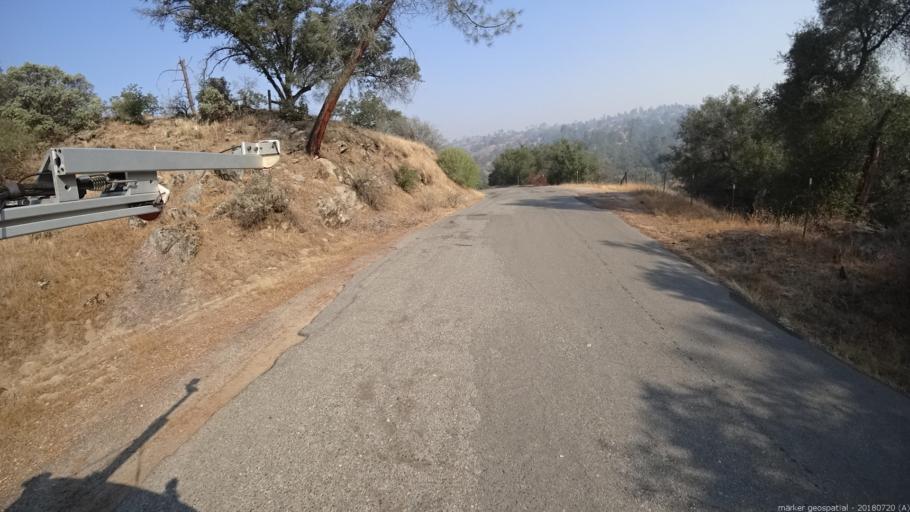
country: US
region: California
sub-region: Madera County
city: Yosemite Lakes
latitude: 37.2726
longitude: -119.8814
